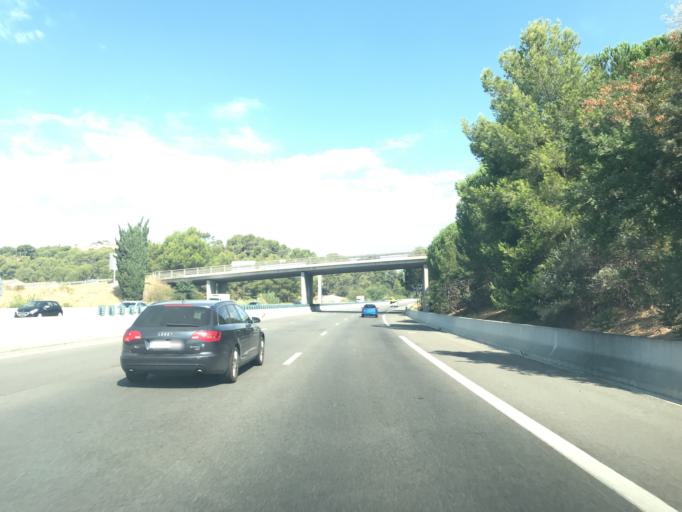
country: FR
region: Provence-Alpes-Cote d'Azur
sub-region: Departement du Var
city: Le Castellet
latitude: 43.1916
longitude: 5.7643
